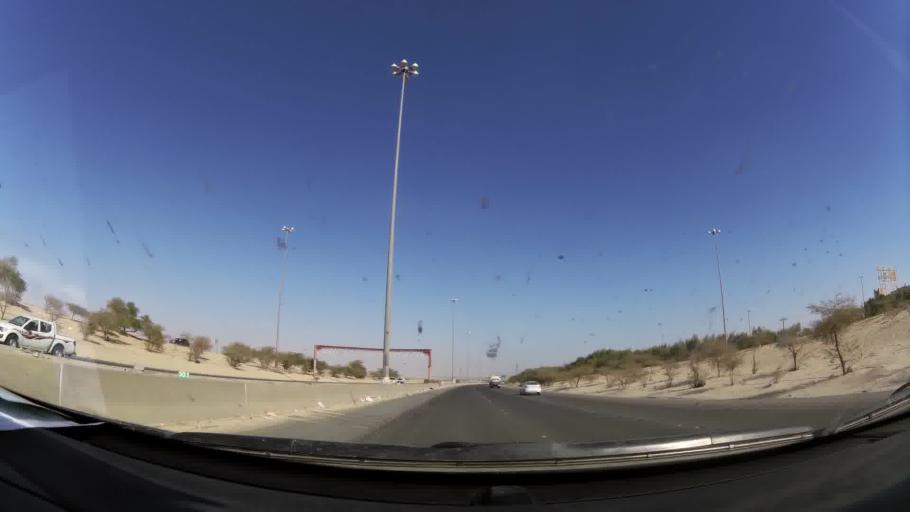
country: KW
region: Muhafazat al Jahra'
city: Al Jahra'
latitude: 29.3656
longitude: 47.6447
